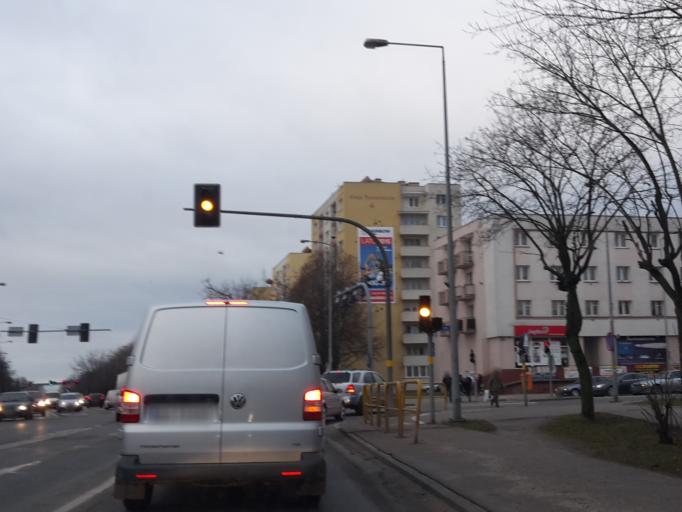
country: PL
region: Warmian-Masurian Voivodeship
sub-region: Powiat elblaski
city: Elblag
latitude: 54.1561
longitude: 19.4051
